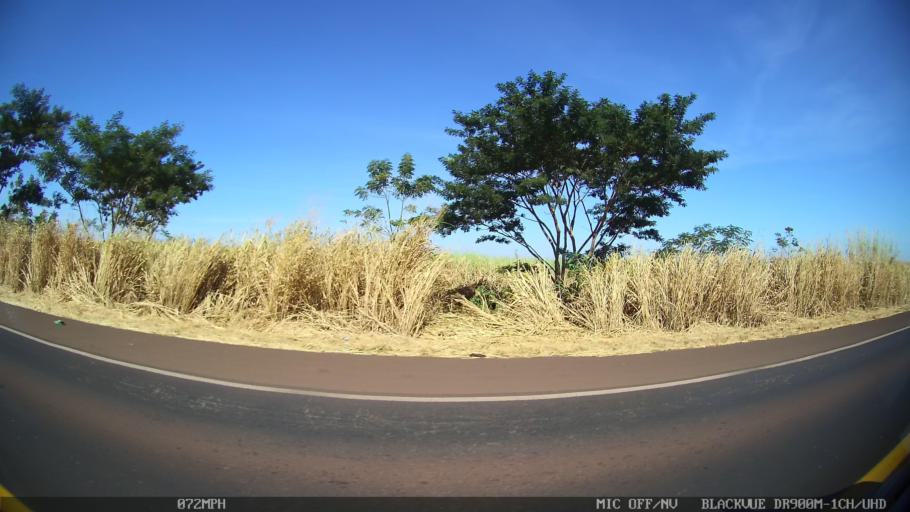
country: BR
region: Sao Paulo
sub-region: Barretos
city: Barretos
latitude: -20.4957
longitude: -48.5315
